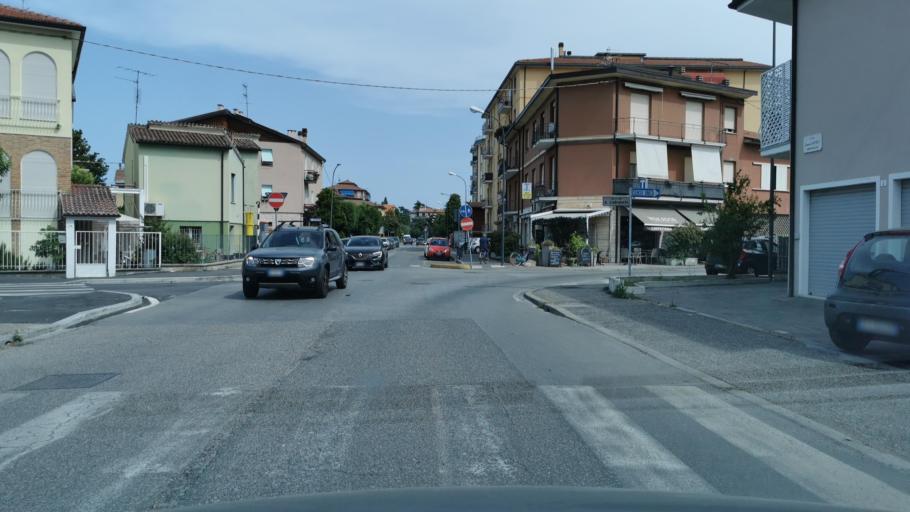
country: IT
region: Emilia-Romagna
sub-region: Provincia di Ravenna
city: Ravenna
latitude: 44.4181
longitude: 12.1819
